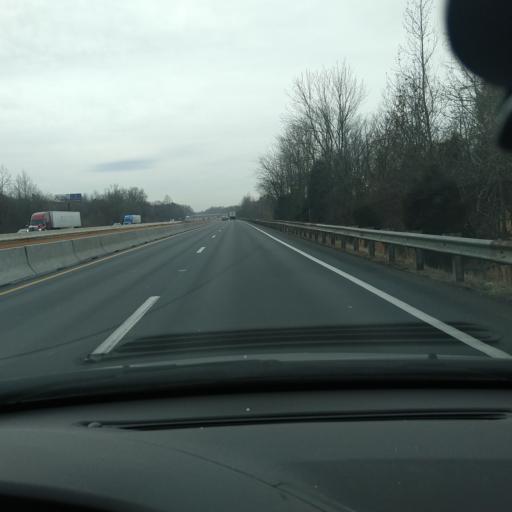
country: US
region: North Carolina
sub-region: Rowan County
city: China Grove
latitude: 35.5490
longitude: -80.5720
